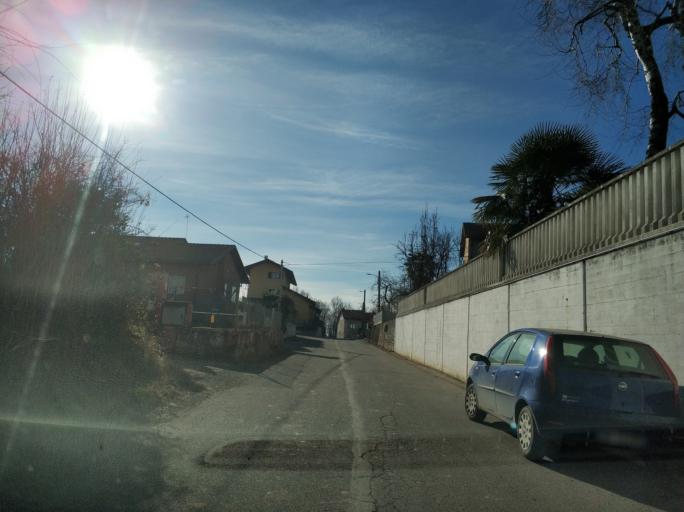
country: IT
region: Piedmont
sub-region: Provincia di Torino
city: San Carlo Canavese
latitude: 45.2508
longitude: 7.5980
